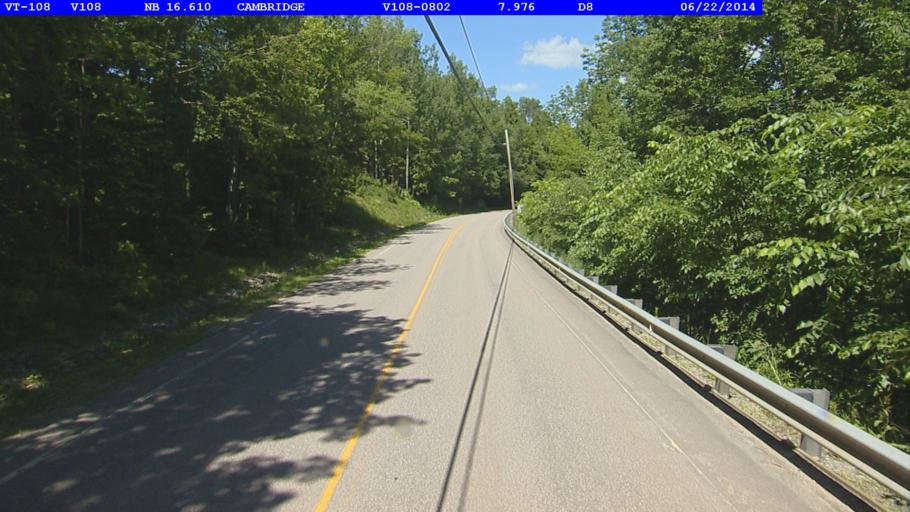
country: US
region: Vermont
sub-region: Lamoille County
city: Johnson
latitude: 44.6336
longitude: -72.8285
